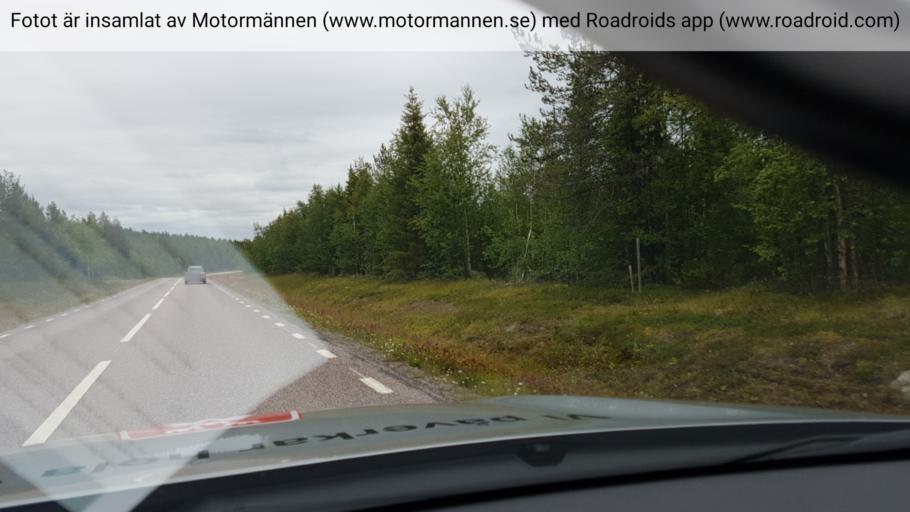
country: SE
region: Norrbotten
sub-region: Gallivare Kommun
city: Gaellivare
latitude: 67.0382
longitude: 21.6681
